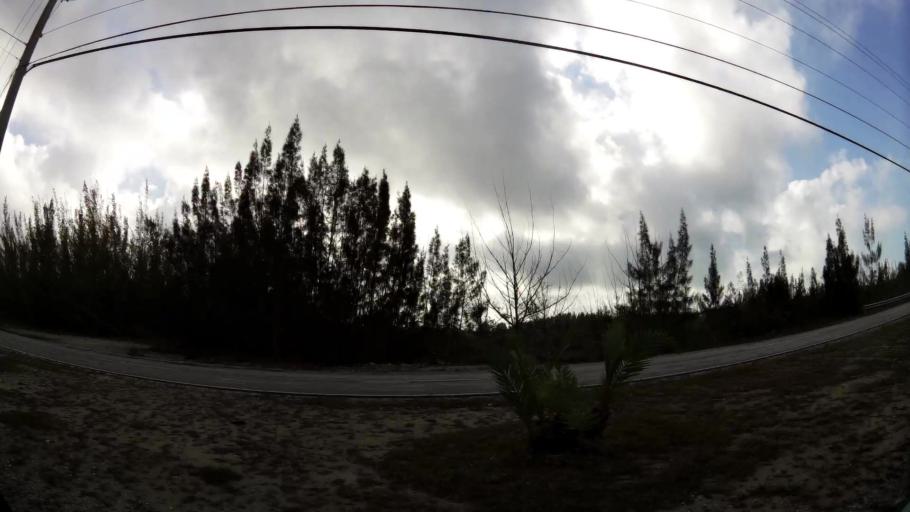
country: BS
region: Freeport
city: Lucaya
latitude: 26.5752
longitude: -78.5813
